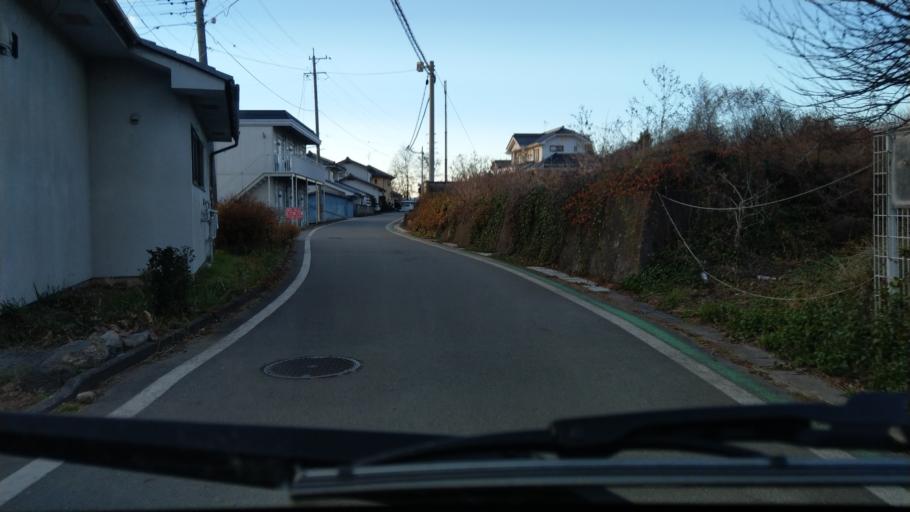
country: JP
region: Nagano
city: Komoro
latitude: 36.3410
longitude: 138.3929
